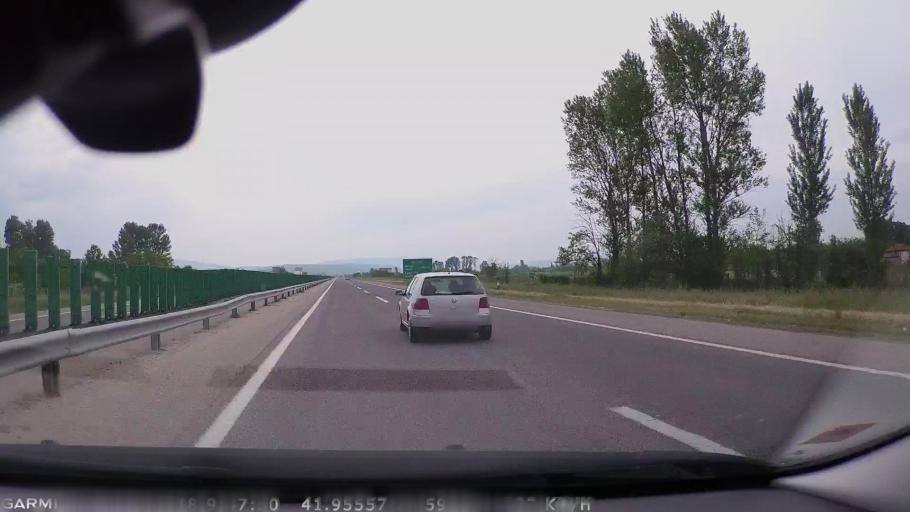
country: MK
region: Ilinden
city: Idrizovo
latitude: 41.9674
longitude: 21.5737
